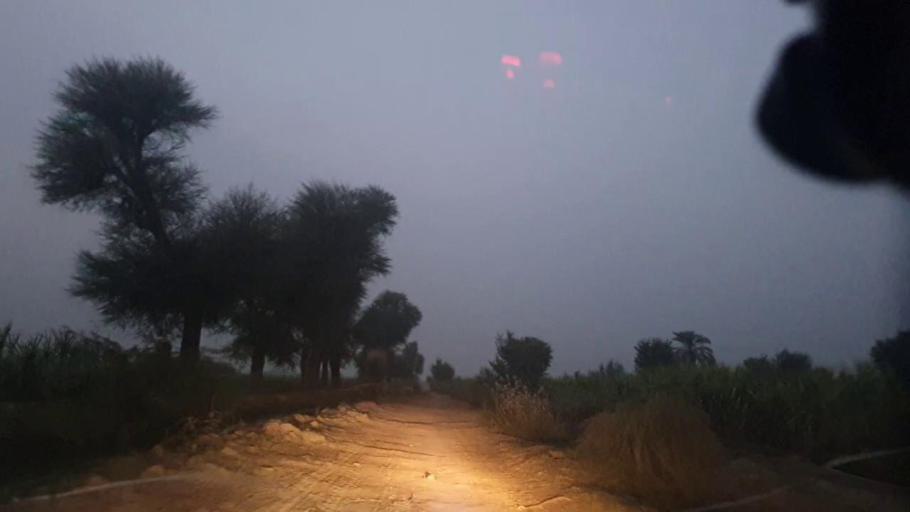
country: PK
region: Sindh
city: Hingorja
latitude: 27.2058
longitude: 68.3715
